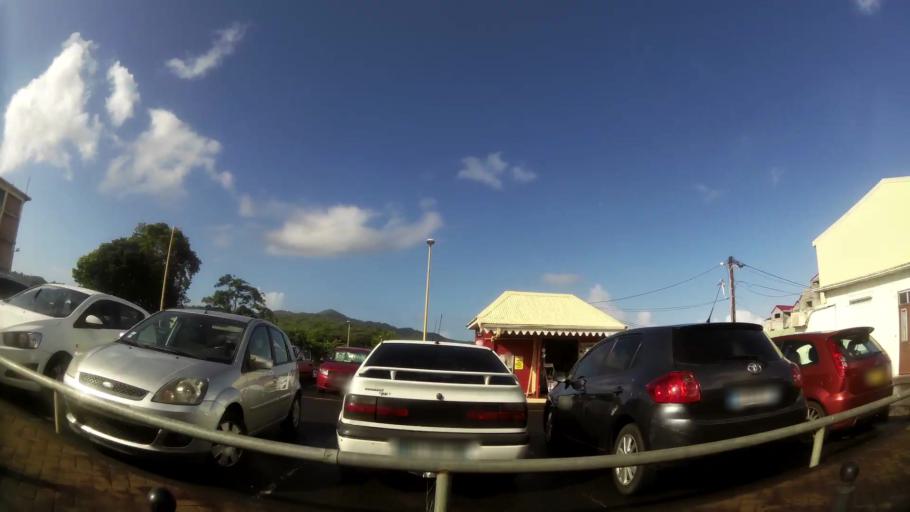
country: MQ
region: Martinique
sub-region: Martinique
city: Ducos
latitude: 14.5293
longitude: -60.9813
